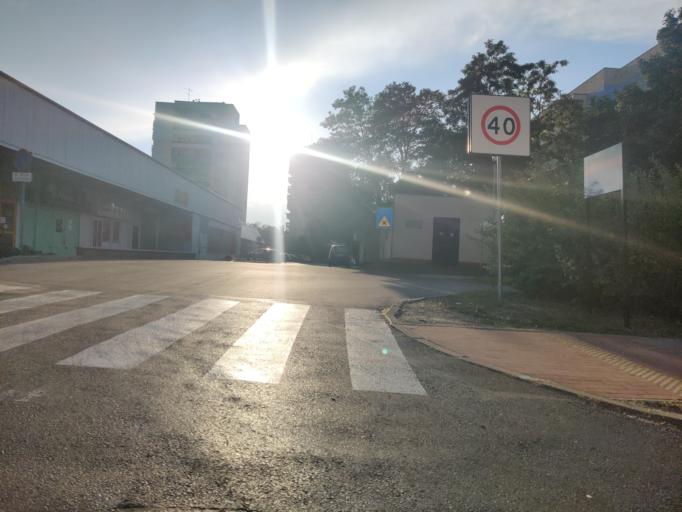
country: PL
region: Greater Poland Voivodeship
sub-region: Konin
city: Konin
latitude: 52.2347
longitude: 18.2607
